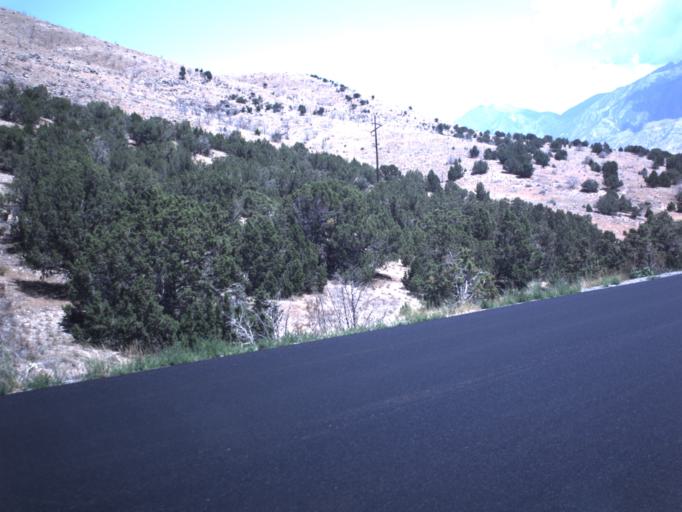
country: US
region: Utah
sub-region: Juab County
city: Nephi
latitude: 39.6980
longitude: -111.9395
